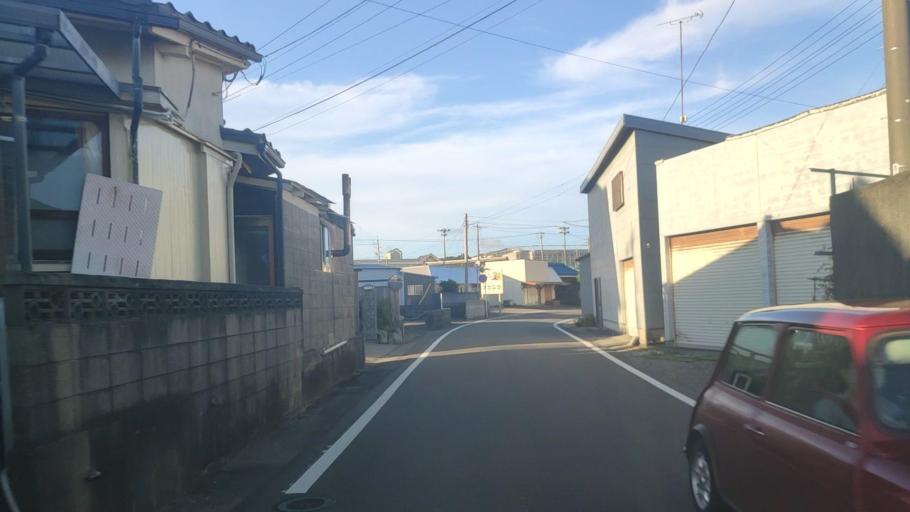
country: JP
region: Mie
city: Toba
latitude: 34.2568
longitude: 136.8100
